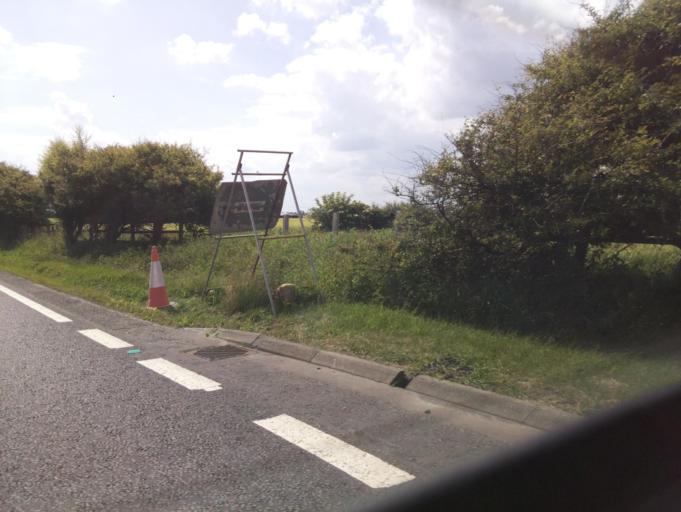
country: GB
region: England
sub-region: Redcar and Cleveland
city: Thornaby-on-Tees
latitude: 54.5138
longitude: -1.2845
